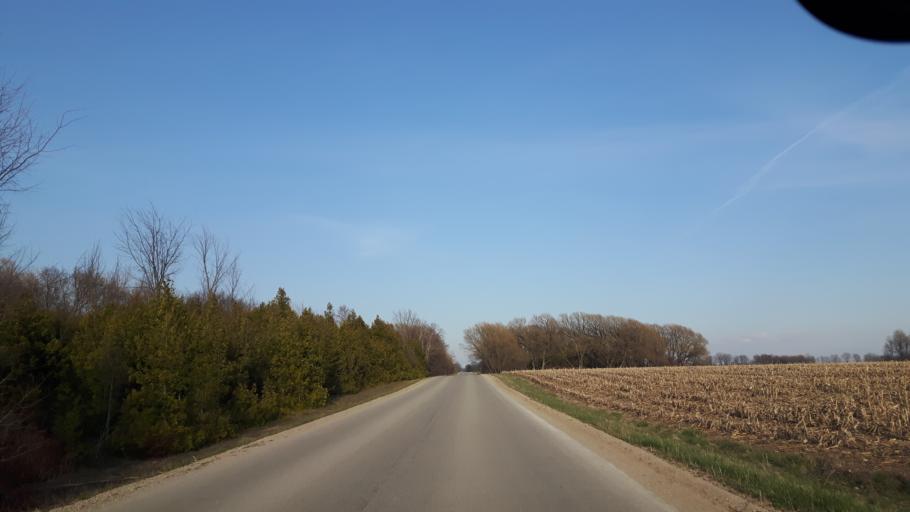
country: CA
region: Ontario
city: Goderich
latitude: 43.6983
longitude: -81.7010
